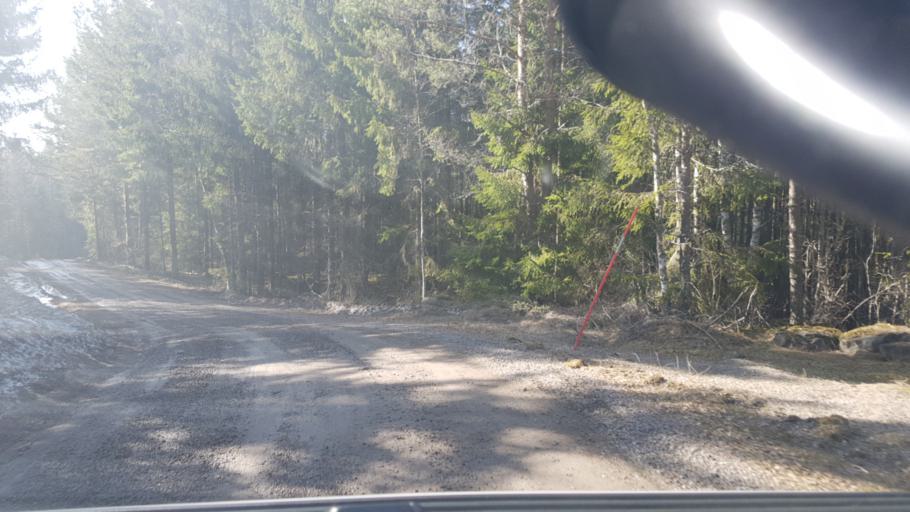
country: SE
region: Vaermland
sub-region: Eda Kommun
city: Amotfors
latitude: 59.8330
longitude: 12.3784
